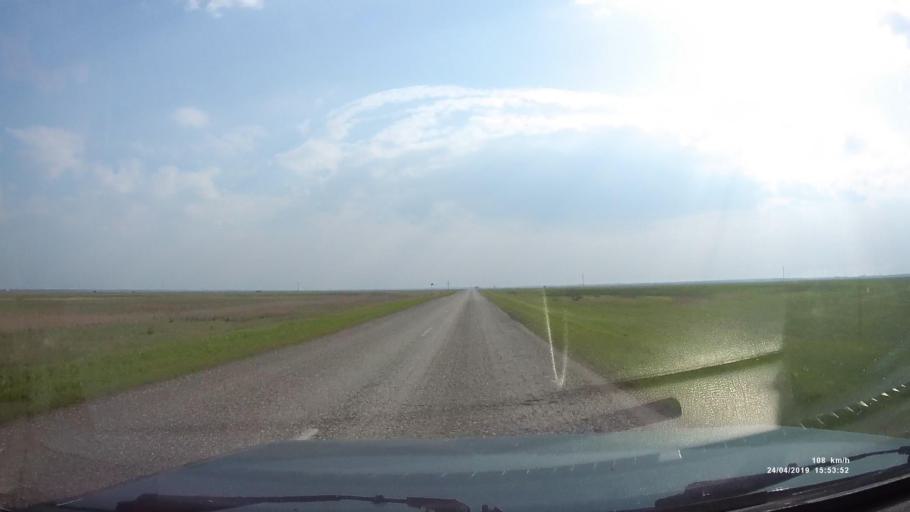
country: RU
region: Kalmykiya
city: Yashalta
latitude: 46.5924
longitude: 42.5699
